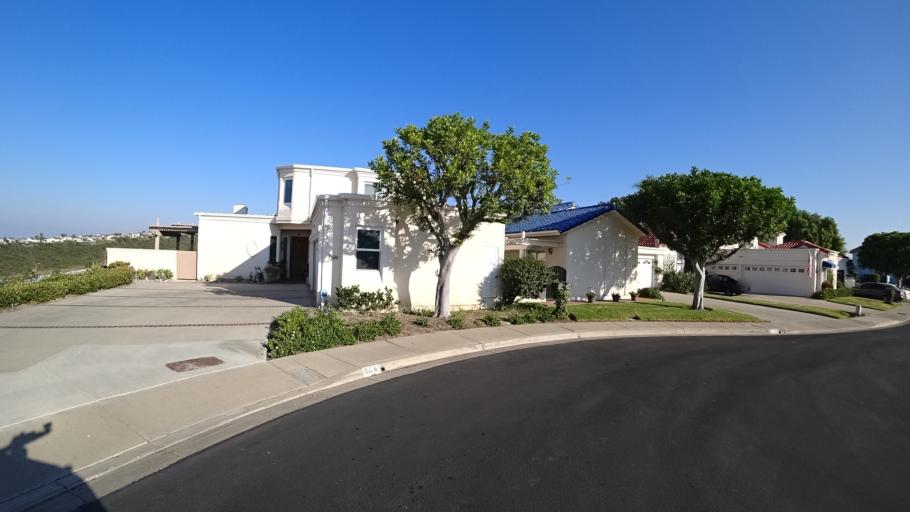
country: US
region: California
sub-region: Orange County
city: San Clemente
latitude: 33.4224
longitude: -117.5923
